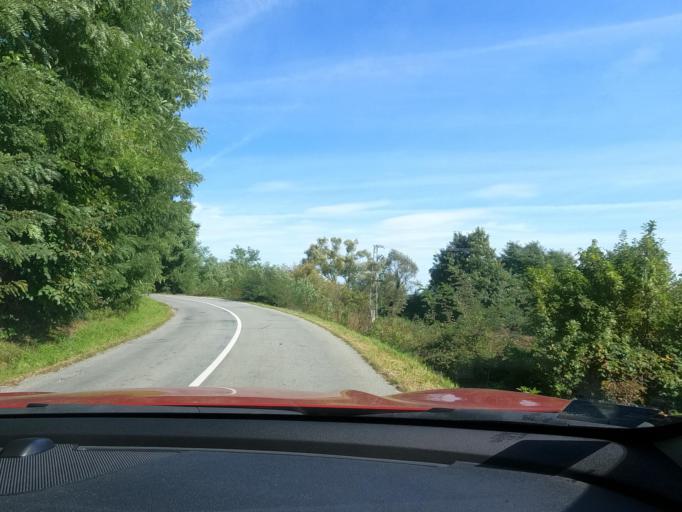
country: HR
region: Sisacko-Moslavacka
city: Petrinja
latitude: 45.3853
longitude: 16.2988
